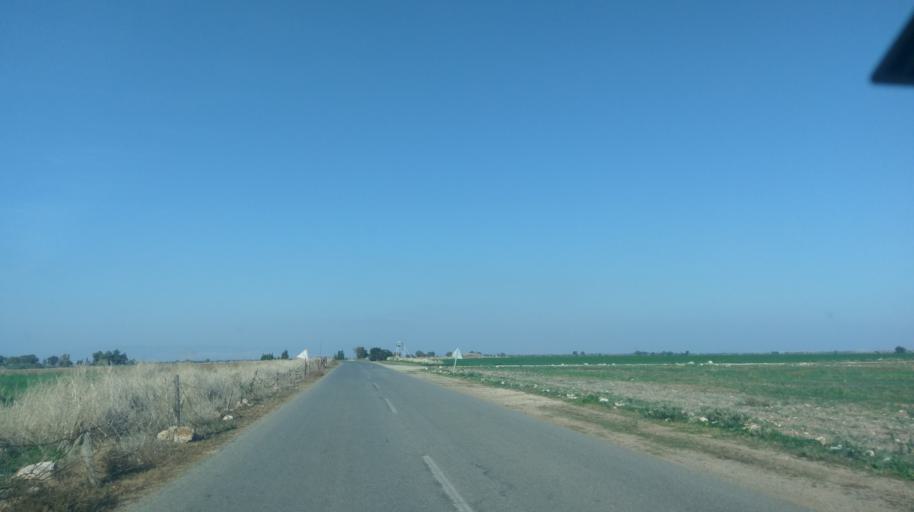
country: CY
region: Larnaka
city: Pergamos
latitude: 35.0674
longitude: 33.7155
